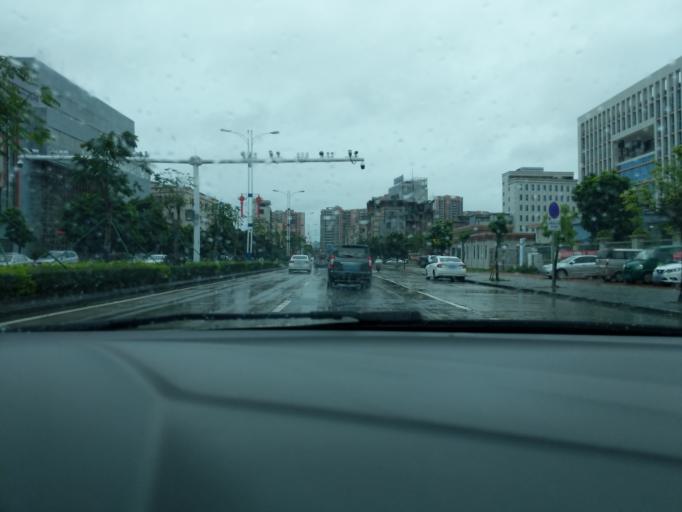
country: CN
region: Guangdong
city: Pingshi
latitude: 22.1988
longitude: 112.3316
